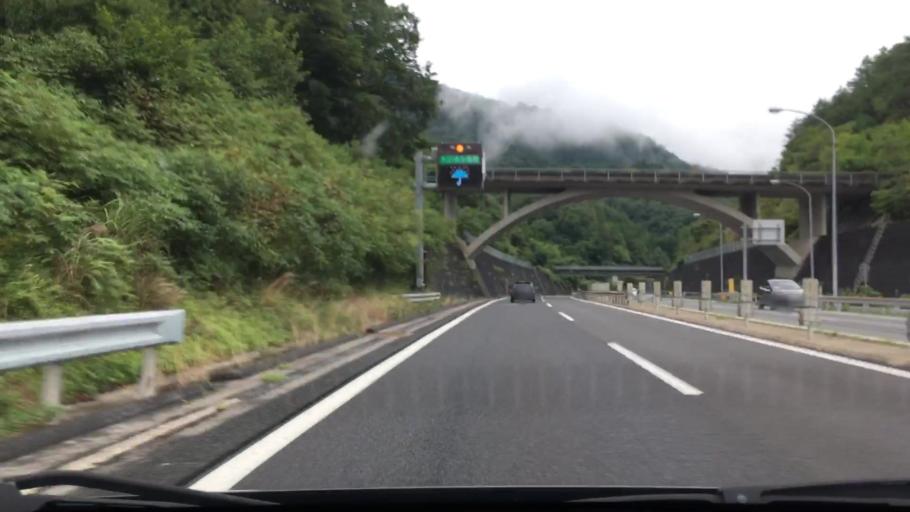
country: JP
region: Hiroshima
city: Hiroshima-shi
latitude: 34.5474
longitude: 132.4522
